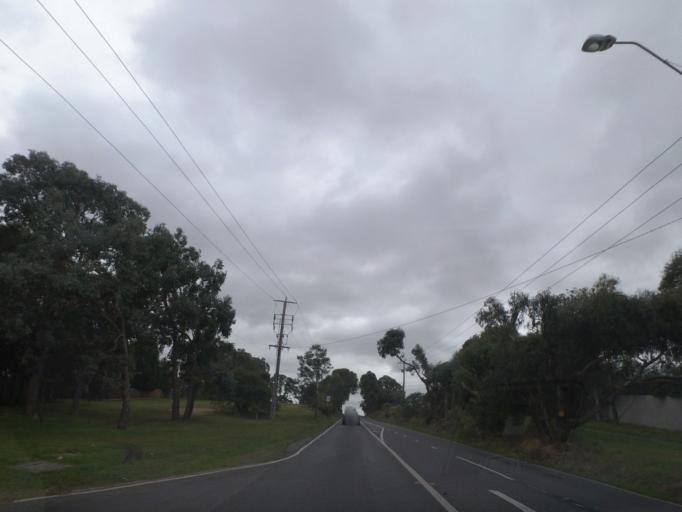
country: AU
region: Victoria
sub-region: Nillumbik
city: Eltham North
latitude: -37.6856
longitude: 145.1431
